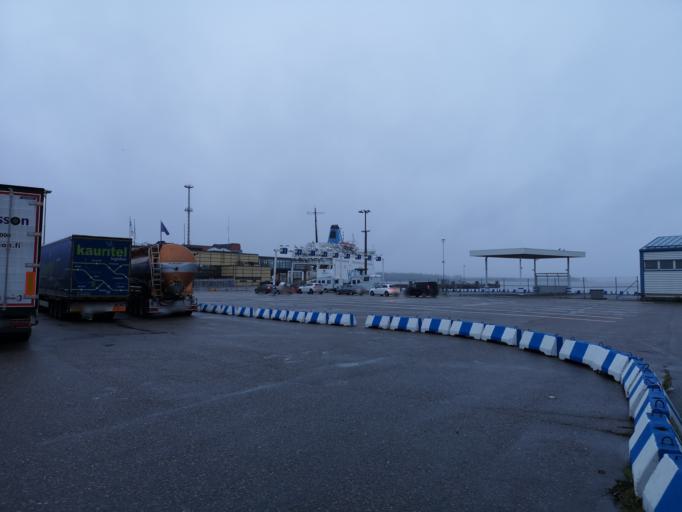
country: FI
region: Ostrobothnia
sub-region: Vaasa
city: Vaasa
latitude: 63.0887
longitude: 21.5580
